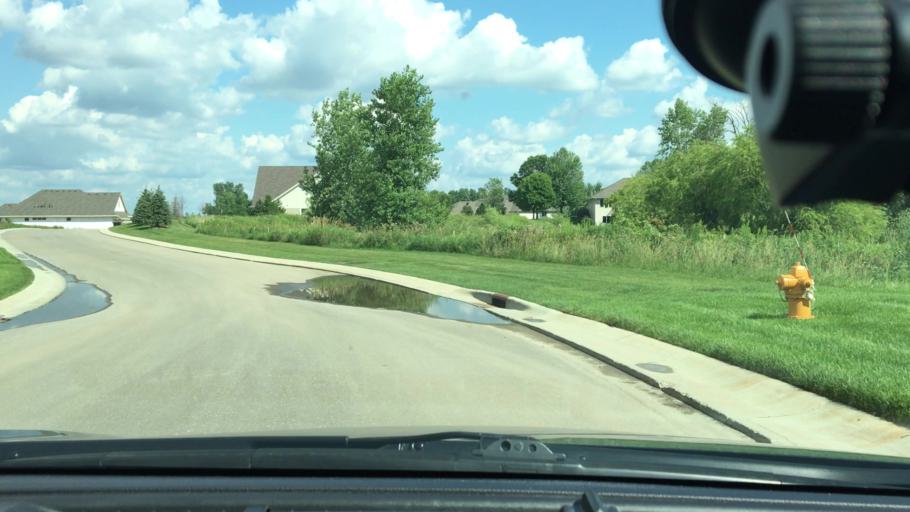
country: US
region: Minnesota
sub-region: Hennepin County
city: New Hope
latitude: 45.0565
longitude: -93.4109
